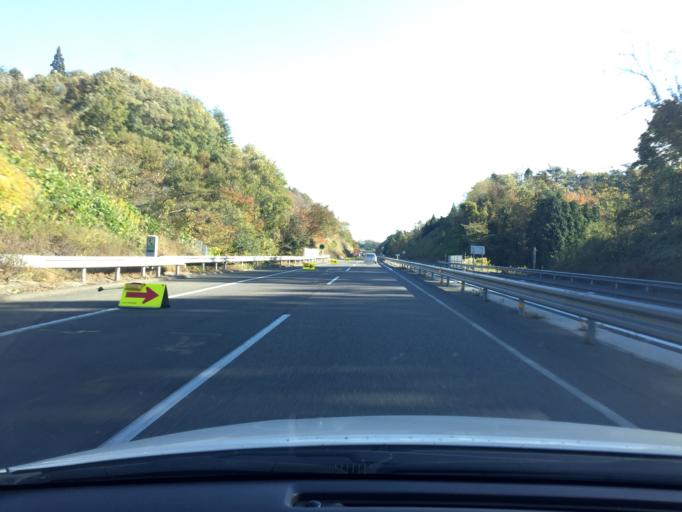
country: JP
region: Fukushima
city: Funehikimachi-funehiki
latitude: 37.4085
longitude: 140.5667
